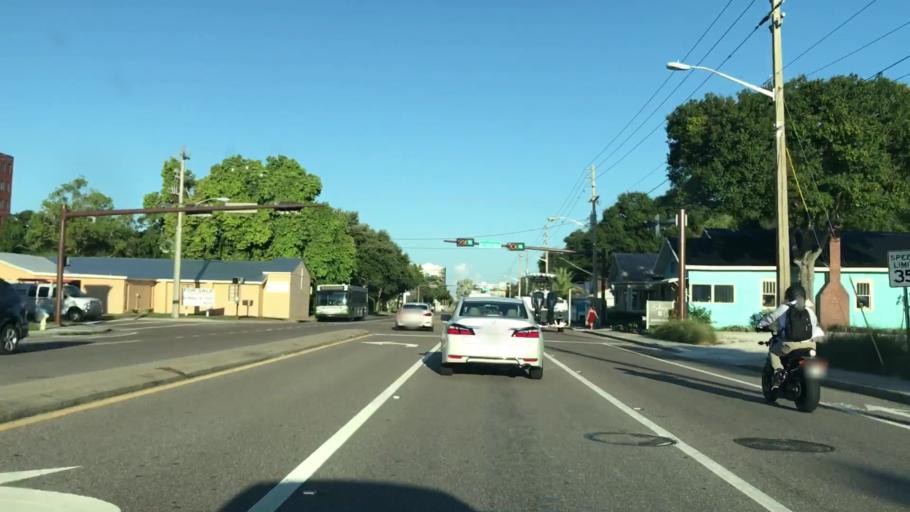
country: US
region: Florida
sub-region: Sarasota County
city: Sarasota
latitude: 27.3389
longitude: -82.5326
